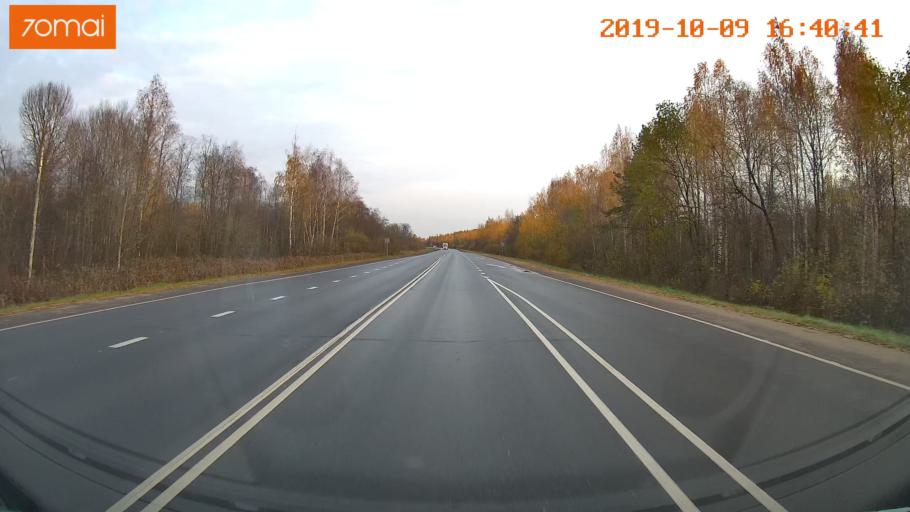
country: RU
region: Kostroma
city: Volgorechensk
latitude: 57.4805
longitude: 41.0651
